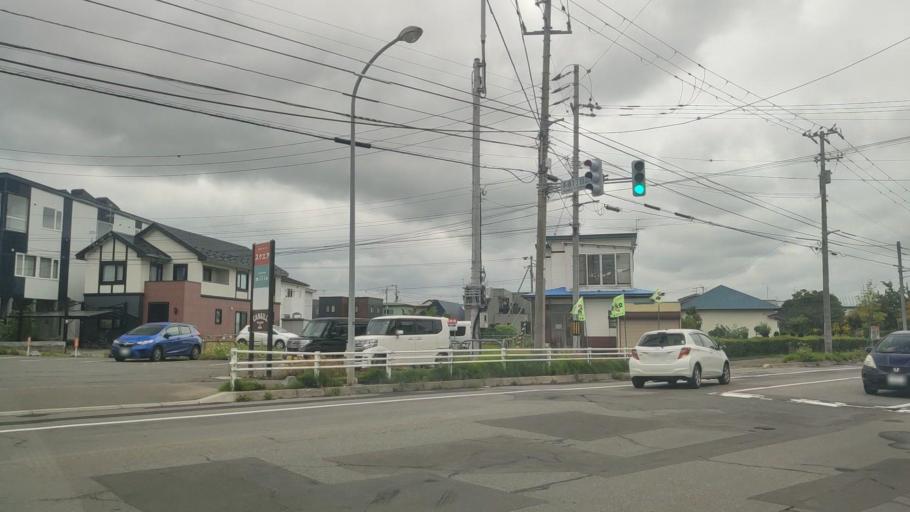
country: JP
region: Hokkaido
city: Hakodate
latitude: 41.7995
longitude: 140.7601
